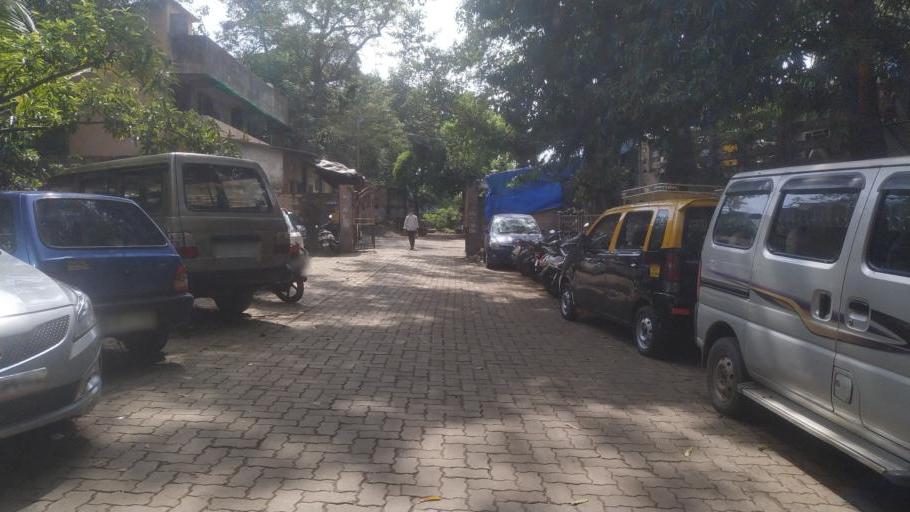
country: IN
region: Maharashtra
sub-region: Mumbai Suburban
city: Mumbai
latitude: 19.0361
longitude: 72.8574
